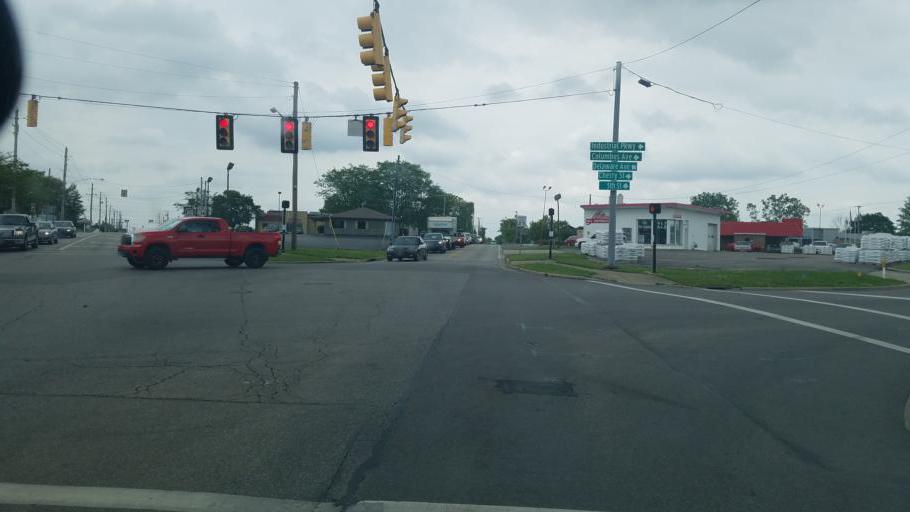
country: US
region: Ohio
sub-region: Union County
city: Marysville
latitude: 40.2357
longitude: -83.3568
